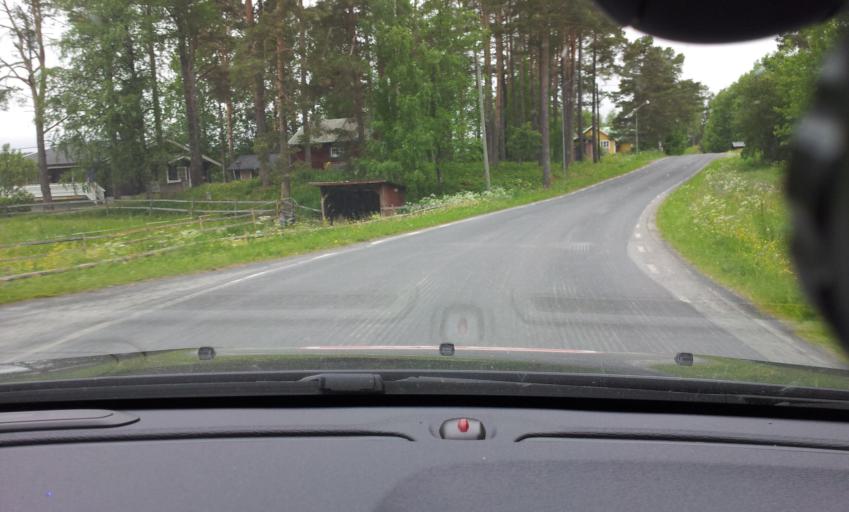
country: SE
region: Jaemtland
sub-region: Krokoms Kommun
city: Valla
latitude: 63.2821
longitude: 13.7602
